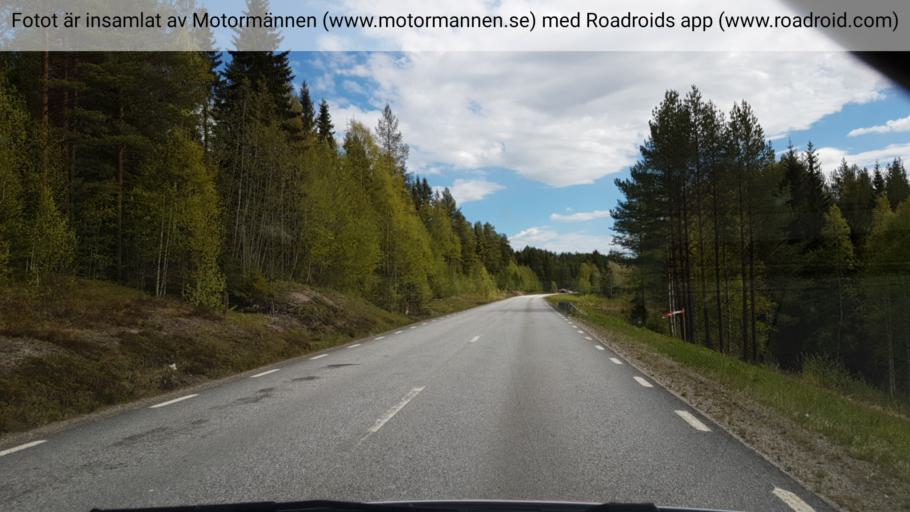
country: SE
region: Vaesterbotten
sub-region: Bjurholms Kommun
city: Bjurholm
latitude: 64.2752
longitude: 19.2561
